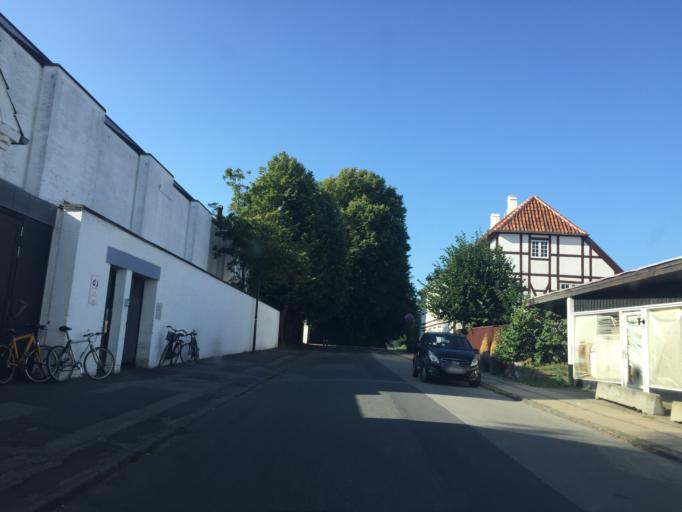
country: DK
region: Capital Region
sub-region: Lyngby-Tarbaek Kommune
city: Kongens Lyngby
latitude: 55.7633
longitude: 12.5363
